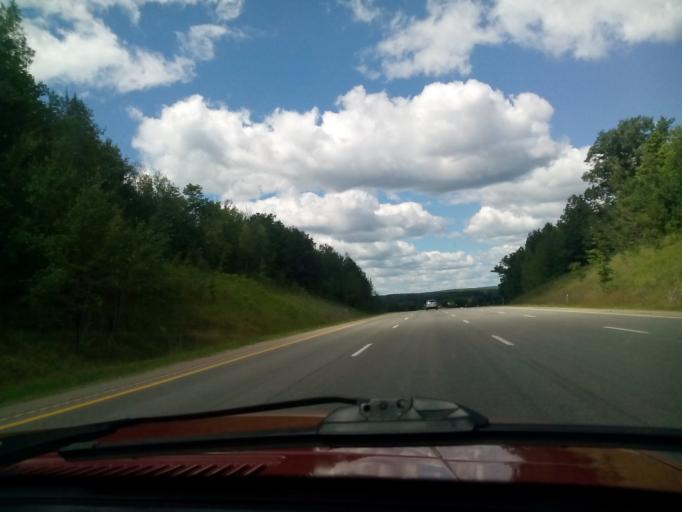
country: US
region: Michigan
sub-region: Ogemaw County
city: West Branch
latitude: 44.2703
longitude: -84.2745
